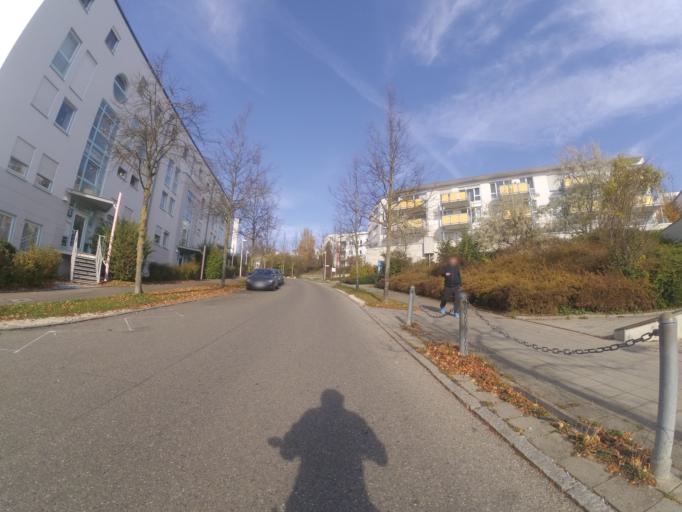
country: DE
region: Baden-Wuerttemberg
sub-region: Tuebingen Region
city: Ulm
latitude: 48.4145
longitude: 9.9450
